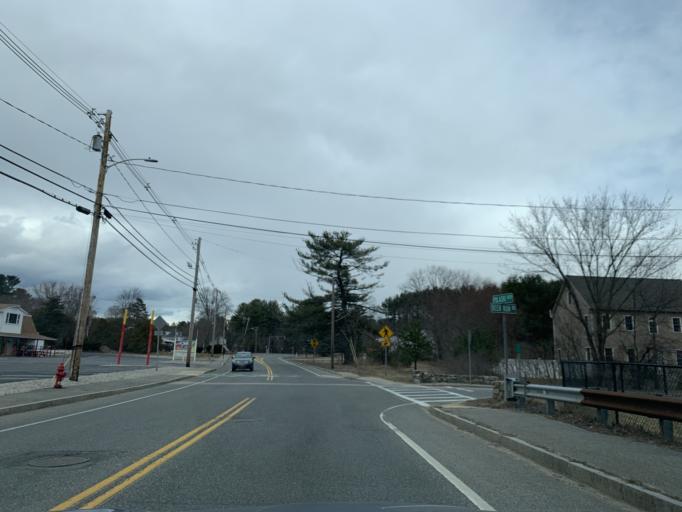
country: US
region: Rhode Island
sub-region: Providence County
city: Woonsocket
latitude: 42.0351
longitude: -71.4815
